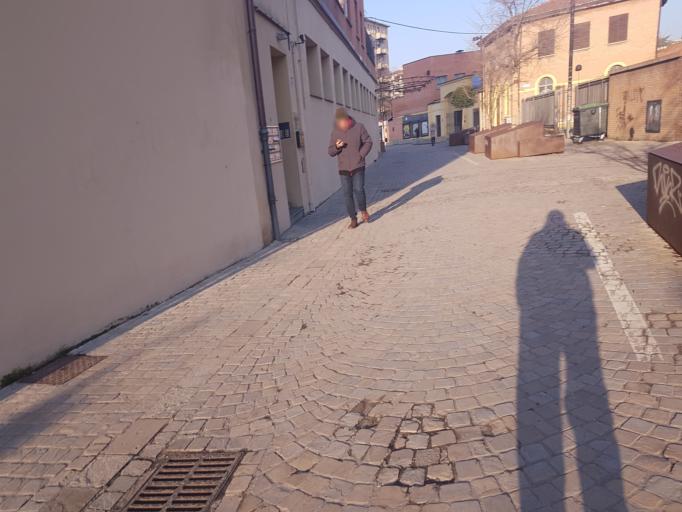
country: IT
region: Emilia-Romagna
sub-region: Provincia di Bologna
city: Bologna
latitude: 44.5017
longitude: 11.3355
